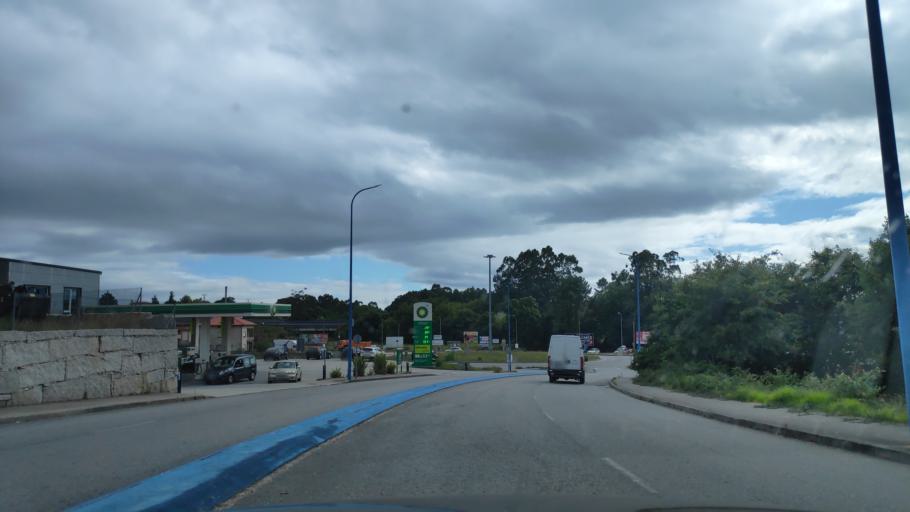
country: ES
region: Galicia
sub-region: Provincia da Coruna
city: Rianxo
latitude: 42.6700
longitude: -8.8110
